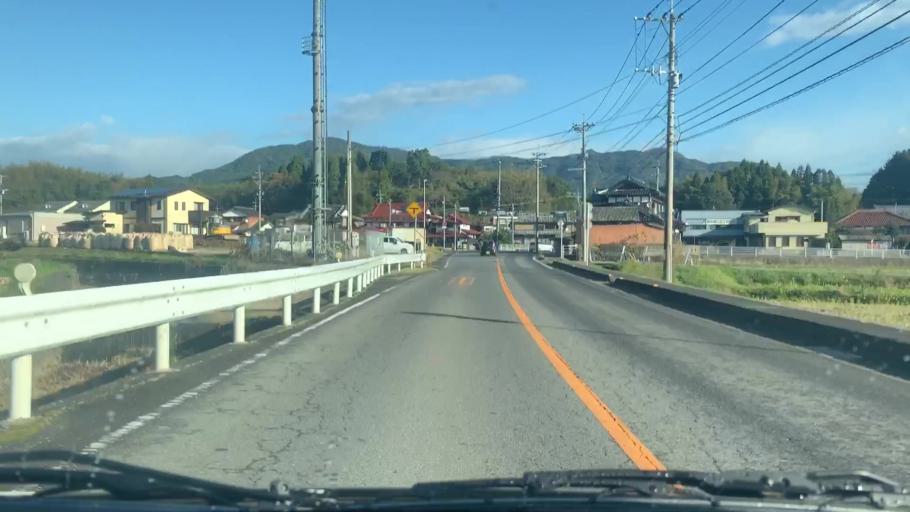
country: JP
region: Saga Prefecture
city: Takeocho-takeo
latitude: 33.2206
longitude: 130.0278
